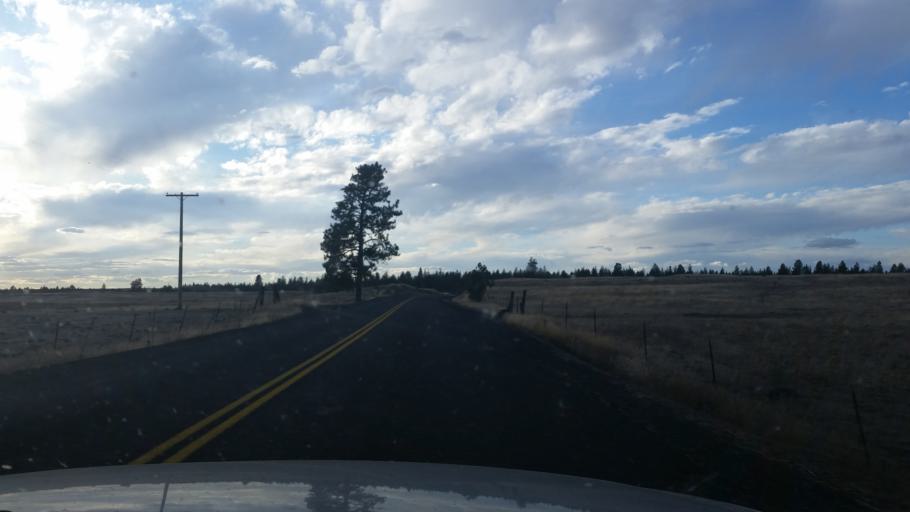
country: US
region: Washington
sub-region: Spokane County
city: Medical Lake
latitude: 47.4506
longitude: -117.7971
